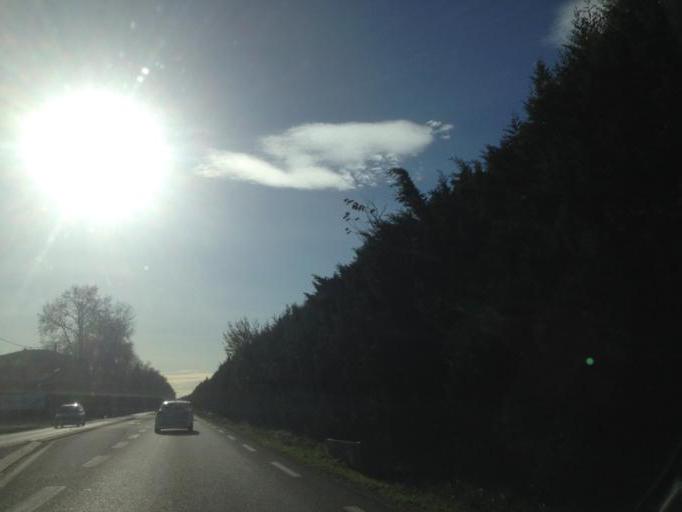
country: FR
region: Provence-Alpes-Cote d'Azur
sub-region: Departement du Vaucluse
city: Courthezon
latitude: 44.0790
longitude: 4.8807
